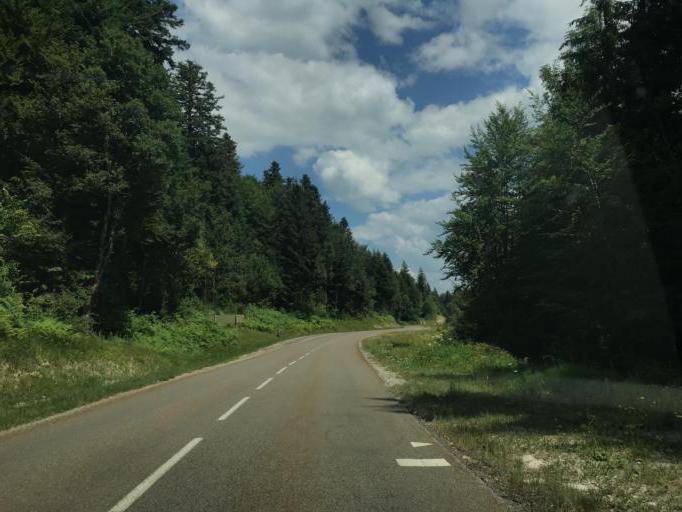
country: FR
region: Franche-Comte
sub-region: Departement du Jura
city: Clairvaux-les-Lacs
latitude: 46.5313
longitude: 5.7910
